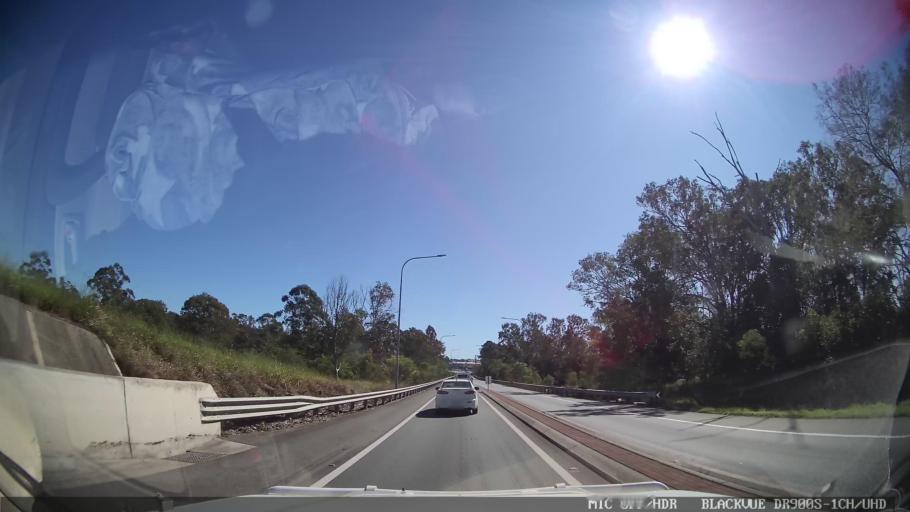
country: AU
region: Queensland
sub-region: Gympie Regional Council
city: Monkland
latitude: -26.2347
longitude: 152.6985
